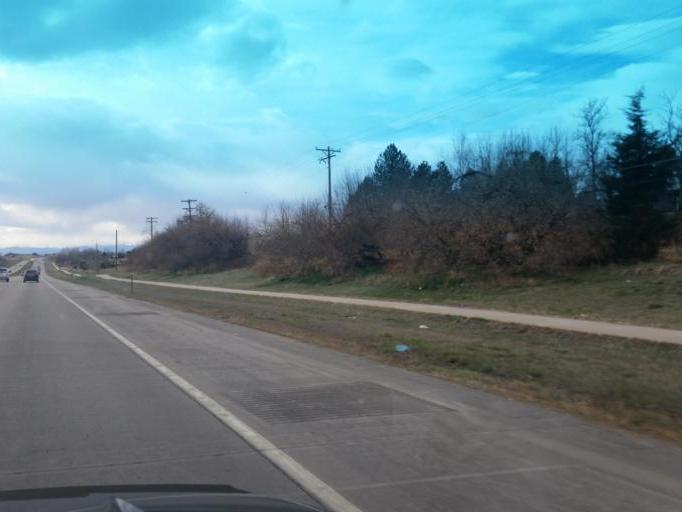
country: US
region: Colorado
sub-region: Weld County
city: Greeley
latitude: 40.3922
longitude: -104.7636
